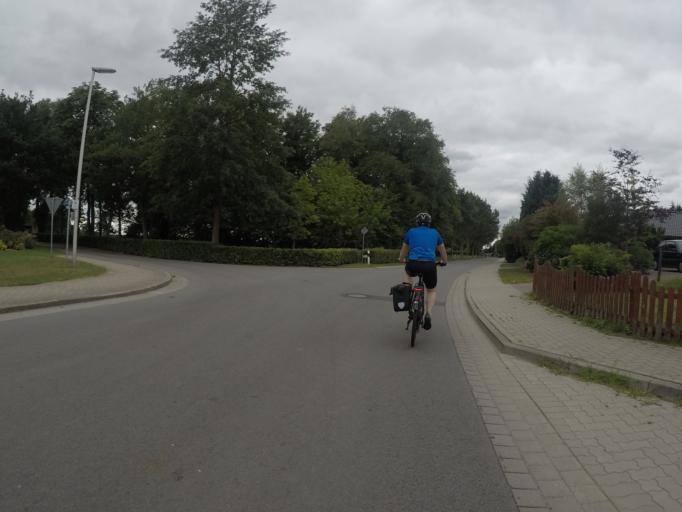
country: DE
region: Lower Saxony
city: Hemmoor
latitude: 53.6974
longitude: 9.1100
